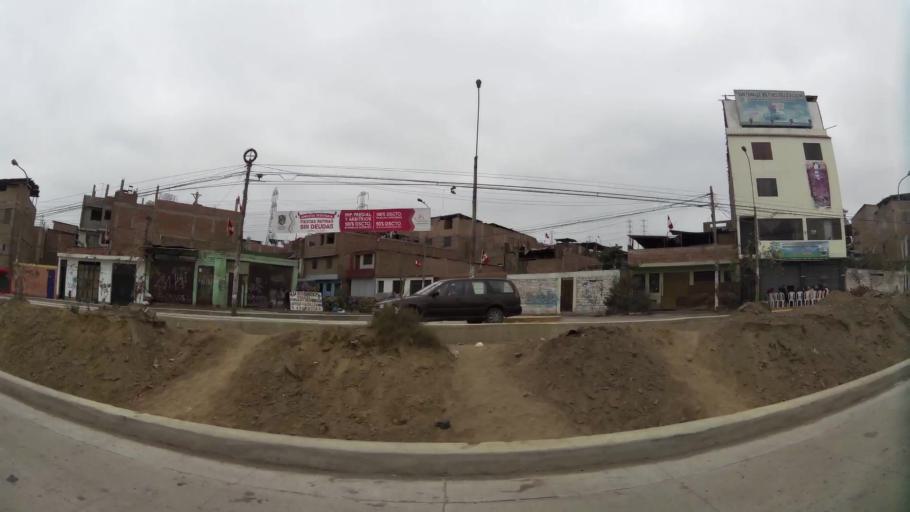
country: PE
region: Lima
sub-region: Lima
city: Surco
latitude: -12.1829
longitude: -76.9617
